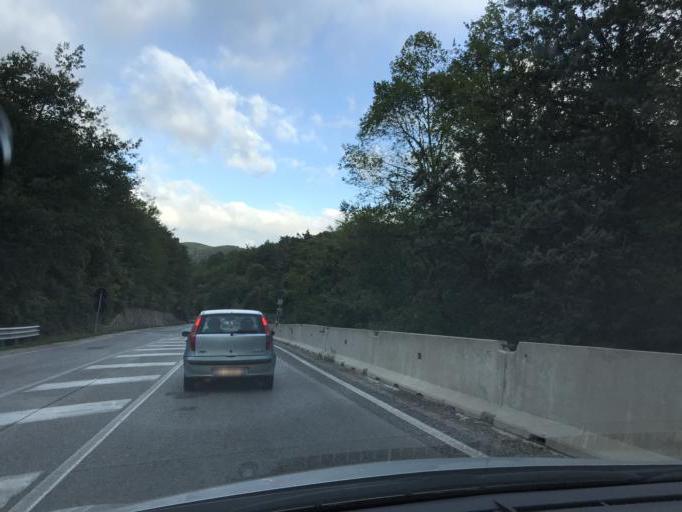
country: IT
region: Umbria
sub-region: Provincia di Terni
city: Ferentillo
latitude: 42.6677
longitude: 12.7349
